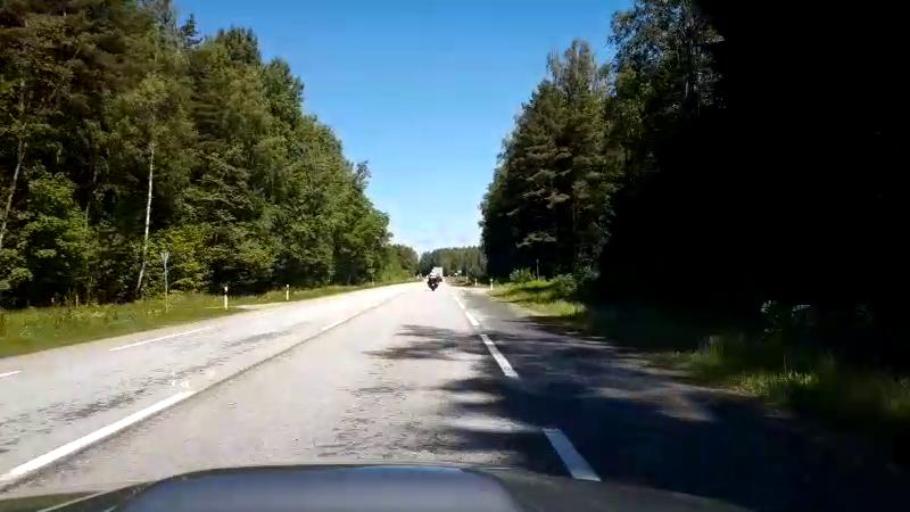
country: LV
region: Saulkrastu
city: Saulkrasti
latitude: 57.4333
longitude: 24.4298
